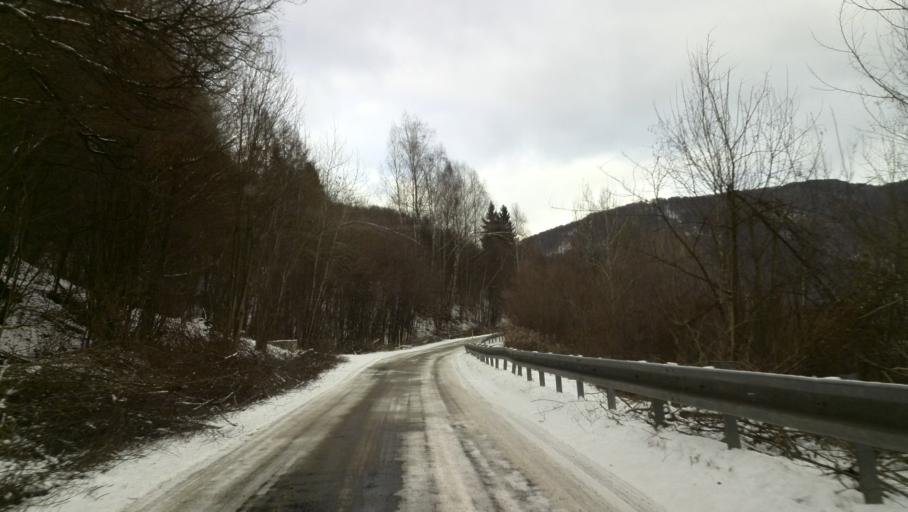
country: SK
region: Kosicky
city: Gelnica
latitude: 48.8263
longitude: 21.0659
